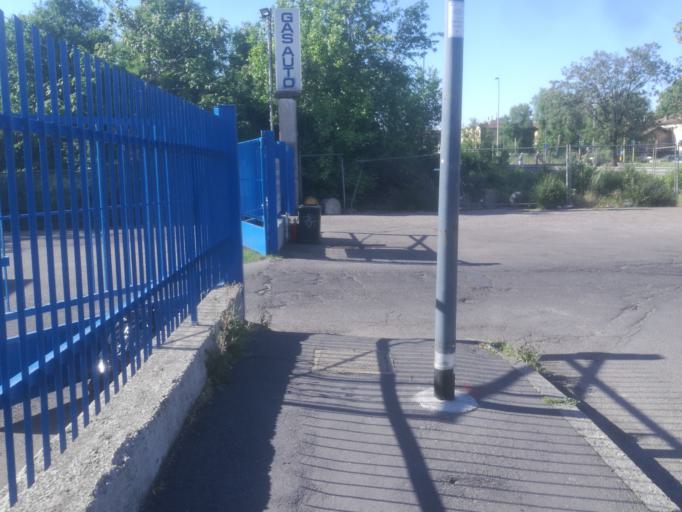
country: IT
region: Lombardy
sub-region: Citta metropolitana di Milano
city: Milano
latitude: 45.4426
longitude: 9.1595
